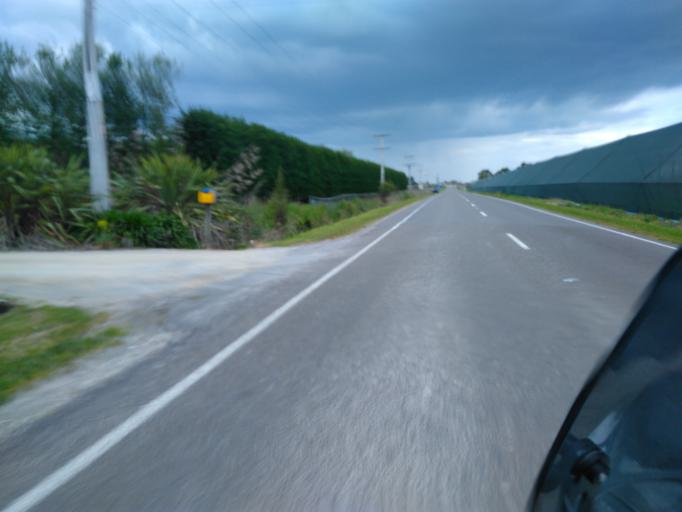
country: NZ
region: Gisborne
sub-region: Gisborne District
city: Gisborne
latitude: -38.6494
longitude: 177.9104
